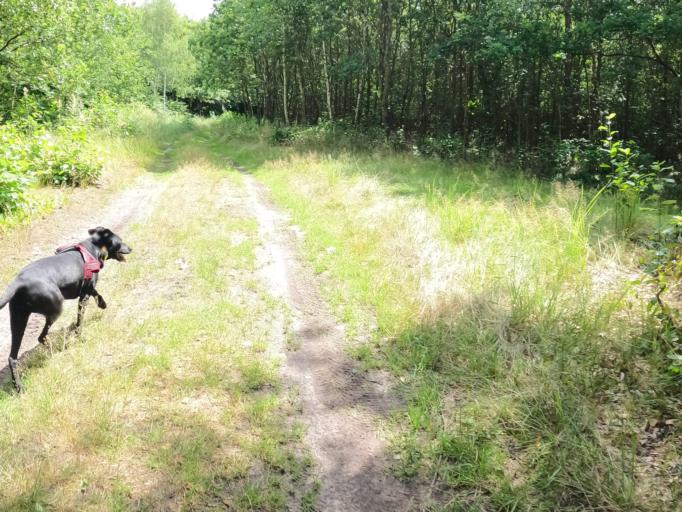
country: PL
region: West Pomeranian Voivodeship
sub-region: Powiat bialogardzki
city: Karlino
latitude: 53.9923
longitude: 15.9235
